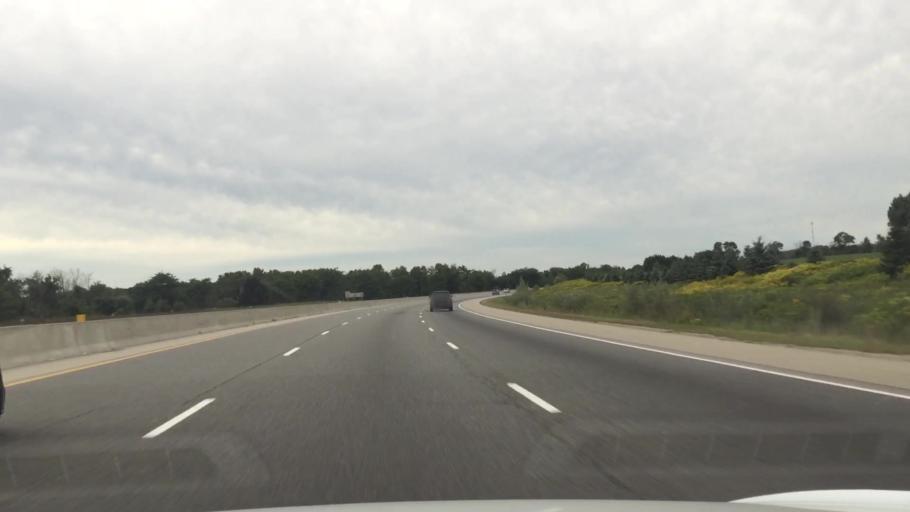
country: CA
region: Ontario
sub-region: Oxford County
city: Woodstock
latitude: 43.2138
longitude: -80.6075
